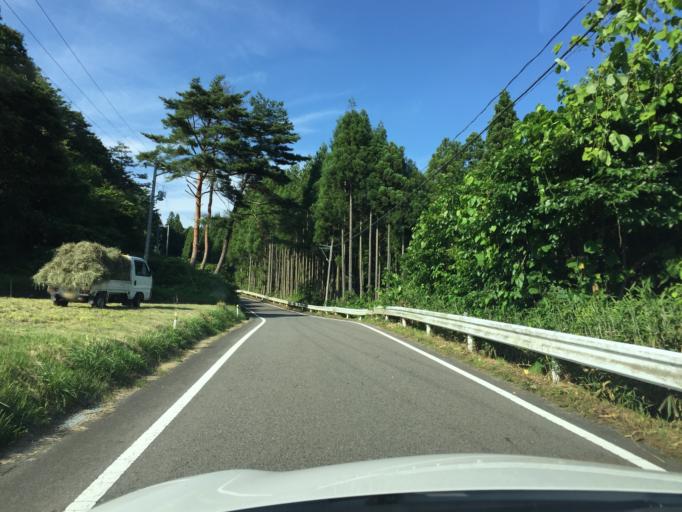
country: JP
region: Fukushima
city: Ishikawa
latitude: 37.2429
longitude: 140.4939
